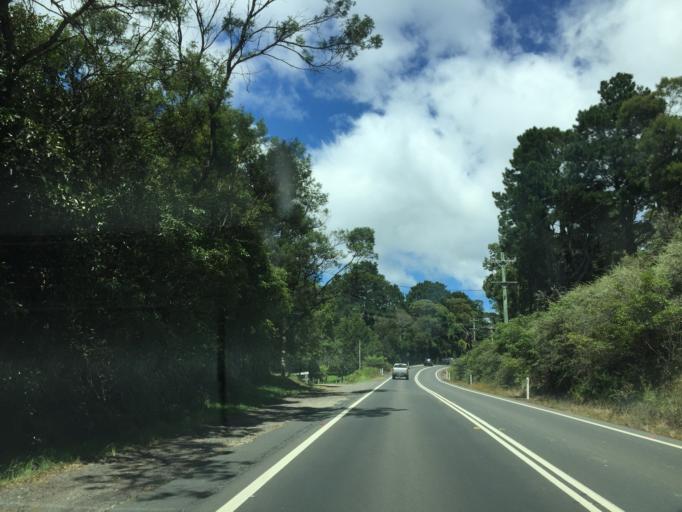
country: AU
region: New South Wales
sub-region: Blue Mountains Municipality
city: Lawson
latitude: -33.5347
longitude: 150.4445
